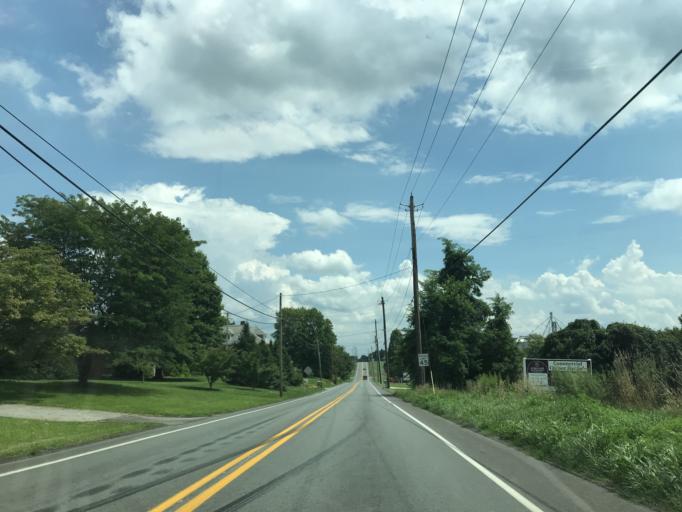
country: US
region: Pennsylvania
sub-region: York County
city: Windsor
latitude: 39.8970
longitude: -76.5681
